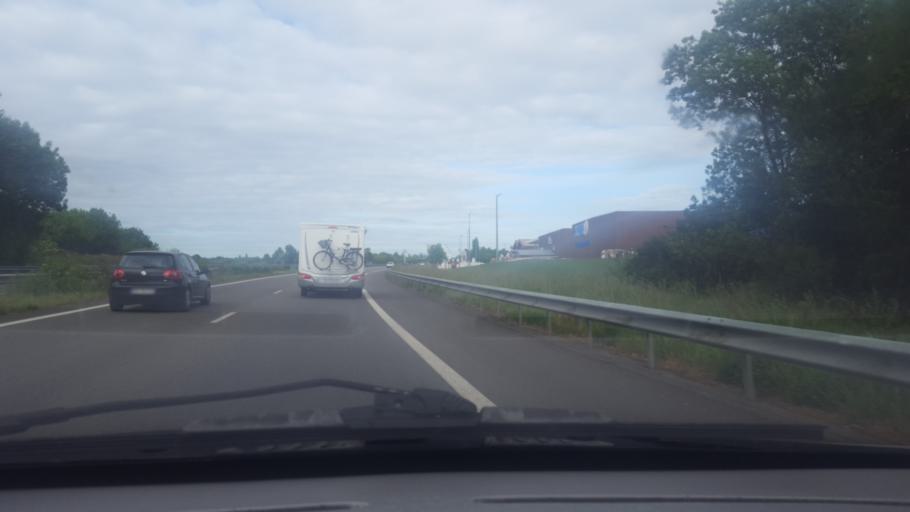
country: FR
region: Pays de la Loire
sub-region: Departement de la Loire-Atlantique
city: Saint-Philbert-de-Grand-Lieu
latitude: 47.0463
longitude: -1.6453
